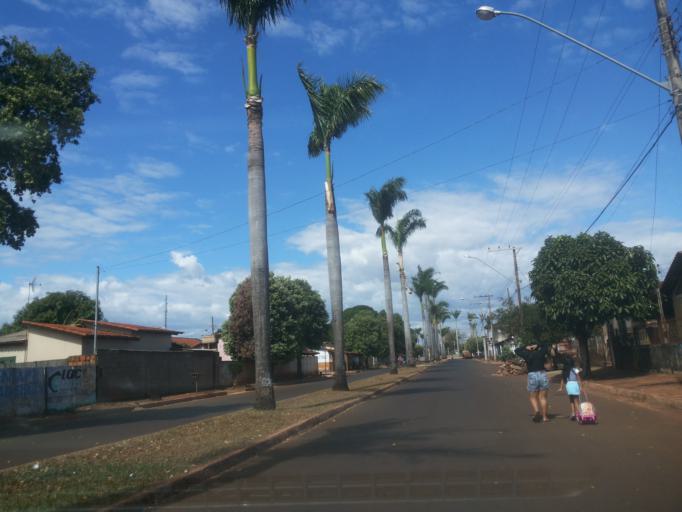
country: BR
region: Minas Gerais
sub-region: Centralina
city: Centralina
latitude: -18.5846
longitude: -49.2016
